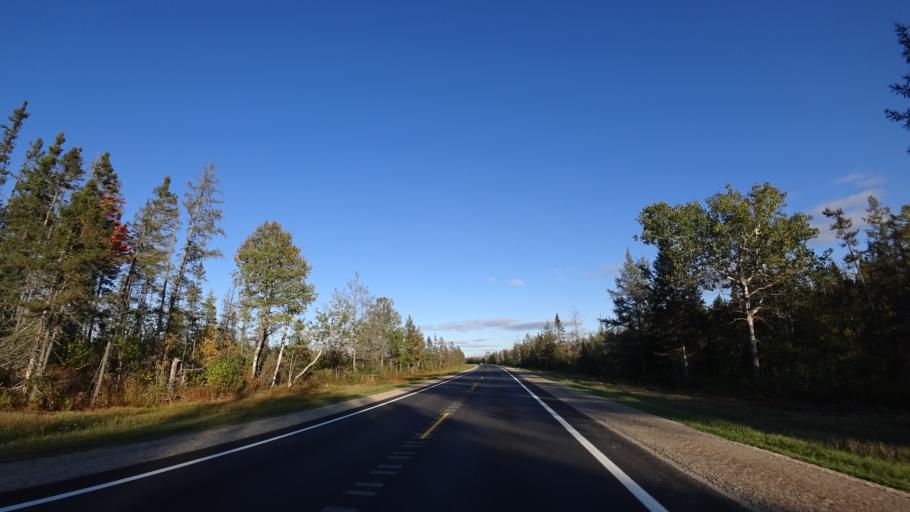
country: US
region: Michigan
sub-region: Luce County
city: Newberry
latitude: 46.3356
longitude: -85.8550
